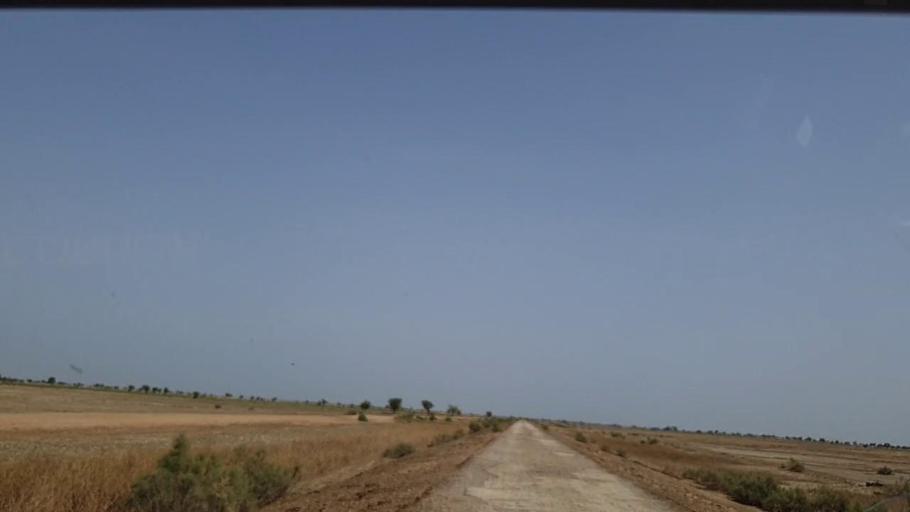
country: PK
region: Sindh
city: Johi
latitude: 26.7813
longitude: 67.6493
